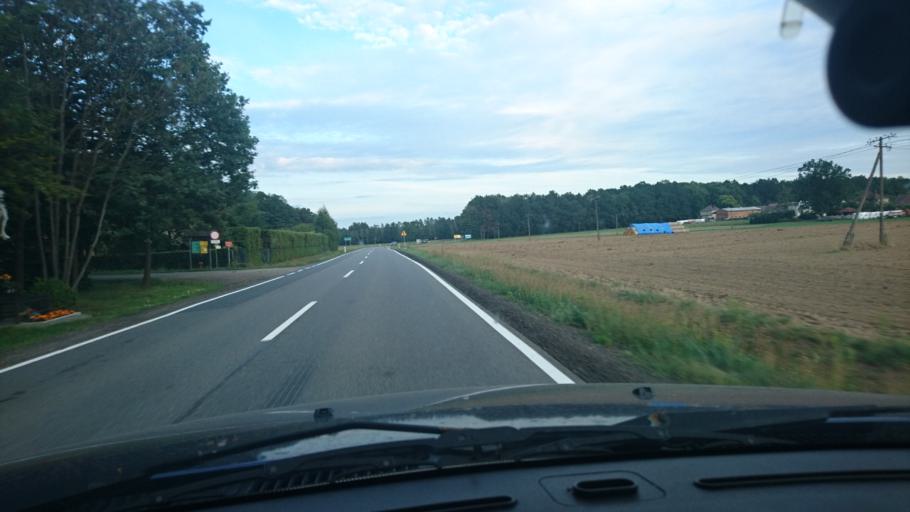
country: PL
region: Opole Voivodeship
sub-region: Powiat oleski
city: Olesno
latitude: 50.8546
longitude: 18.4617
